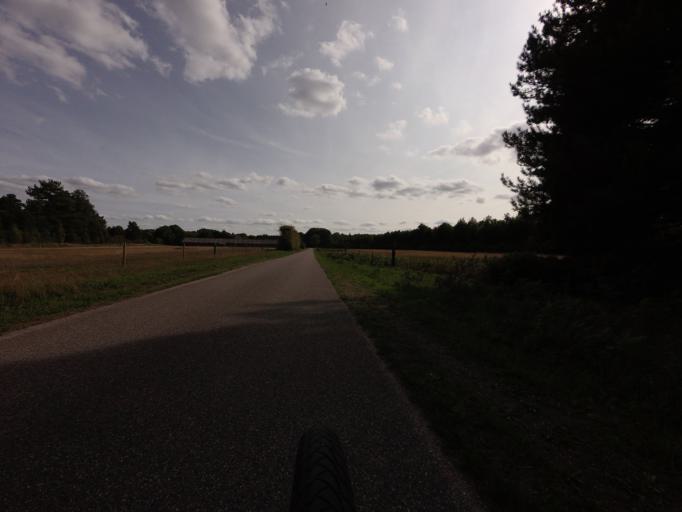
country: DK
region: Zealand
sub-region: Vordingborg Kommune
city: Praesto
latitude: 55.1610
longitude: 12.0923
